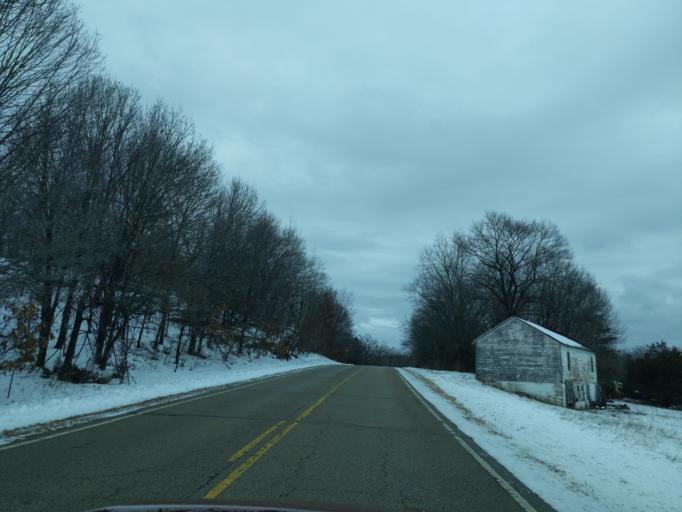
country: US
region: Wisconsin
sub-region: Marquette County
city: Montello
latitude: 43.9180
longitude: -89.3291
